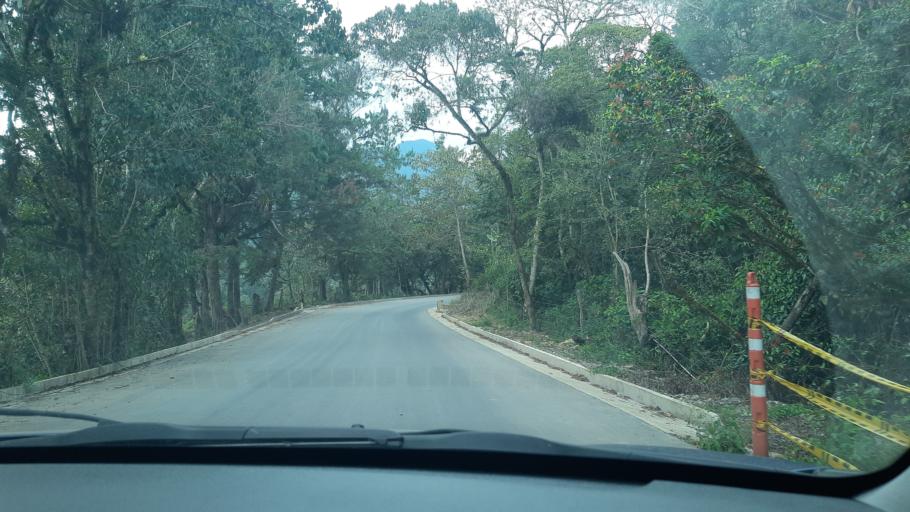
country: CO
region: Boyaca
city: Garagoa
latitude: 5.0883
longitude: -73.3441
